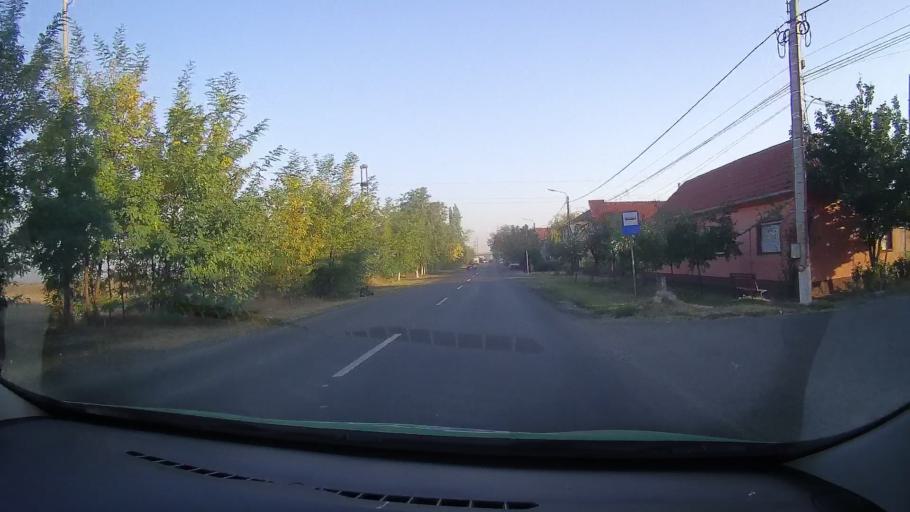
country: RO
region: Arad
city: Arad
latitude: 46.2131
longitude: 21.3206
